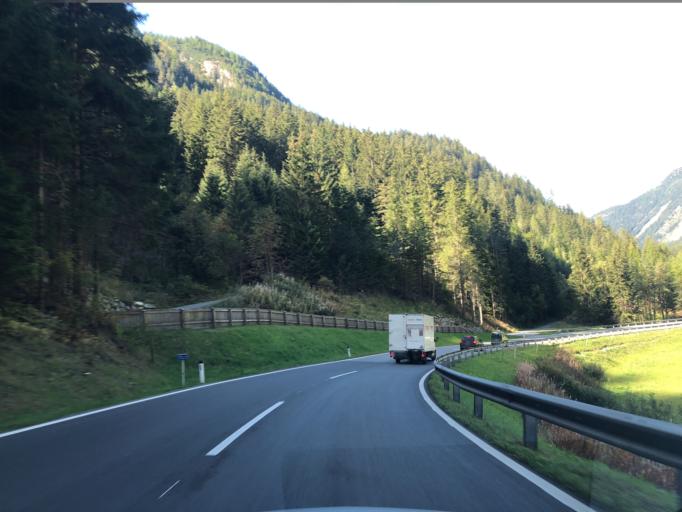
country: AT
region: Tyrol
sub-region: Politischer Bezirk Imst
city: Soelden
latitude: 47.0095
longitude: 11.0020
